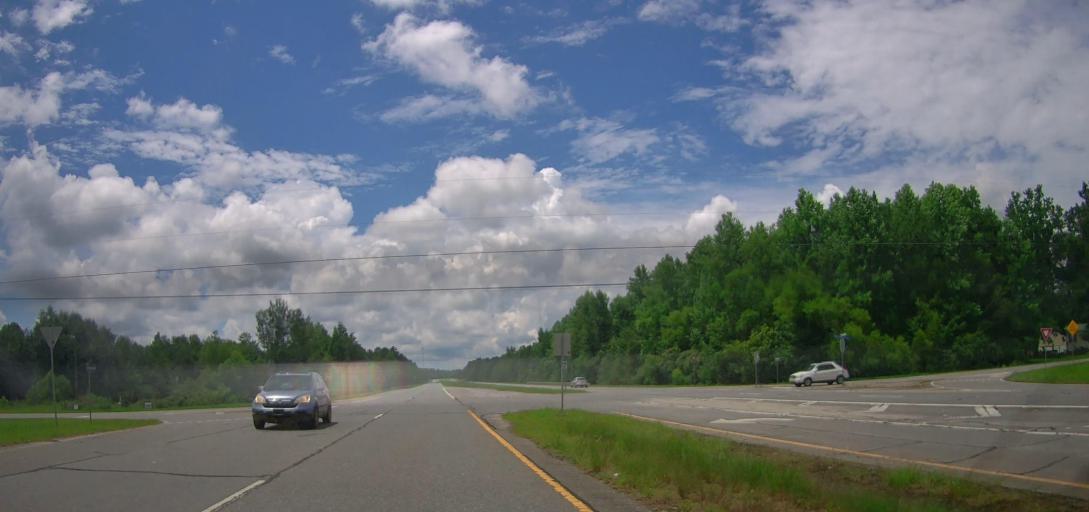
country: US
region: Georgia
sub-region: Dodge County
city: Eastman
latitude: 32.1803
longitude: -83.1917
